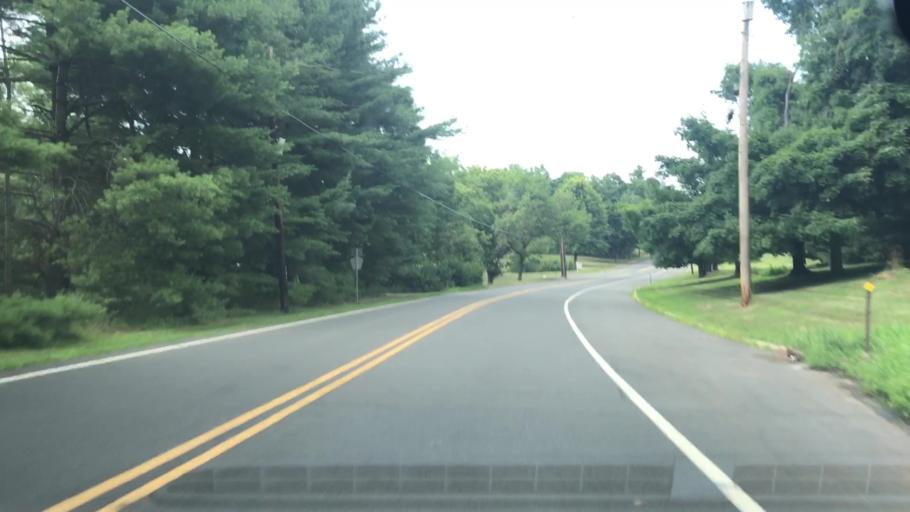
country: US
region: New Jersey
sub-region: Hunterdon County
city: Flemington
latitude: 40.5036
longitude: -74.8089
